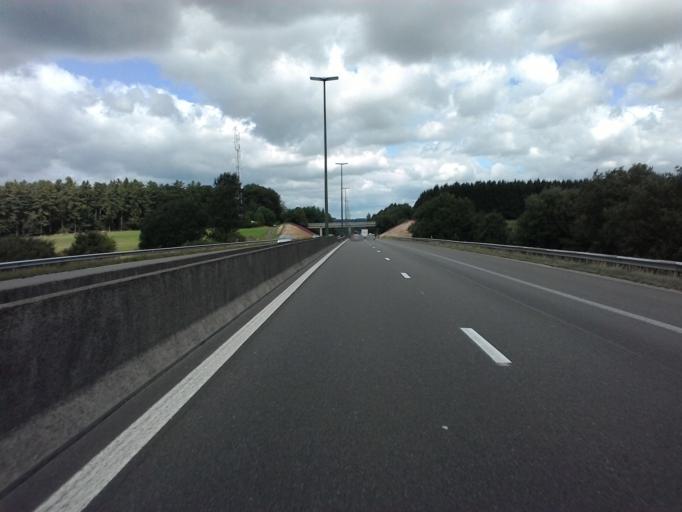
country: BE
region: Wallonia
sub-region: Province du Luxembourg
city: Leglise
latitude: 49.7823
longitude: 5.5371
